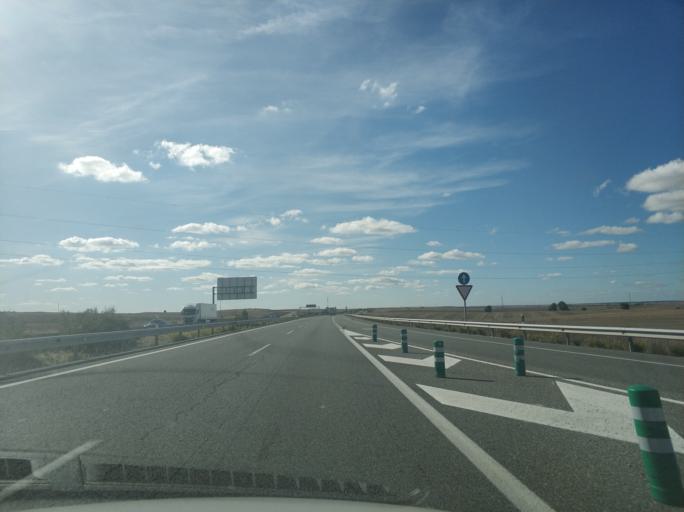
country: ES
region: Castille and Leon
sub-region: Provincia de Burgos
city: Villagonzalo-Pedernales
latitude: 42.3035
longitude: -3.7582
